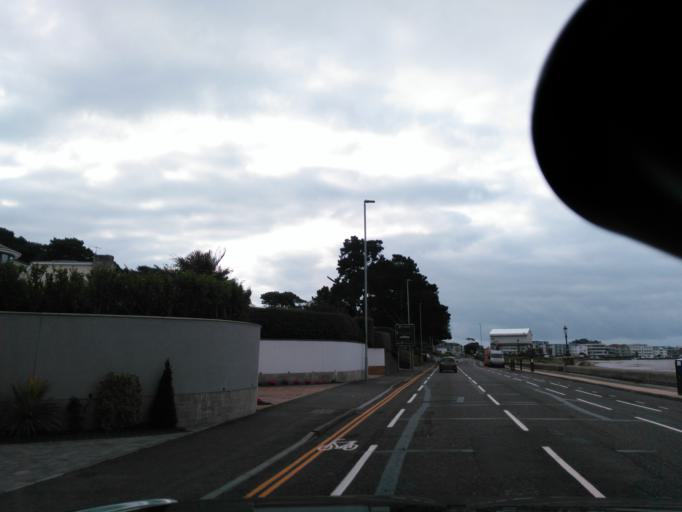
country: GB
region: England
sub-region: Dorset
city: Parkstone
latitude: 50.6996
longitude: -1.9342
